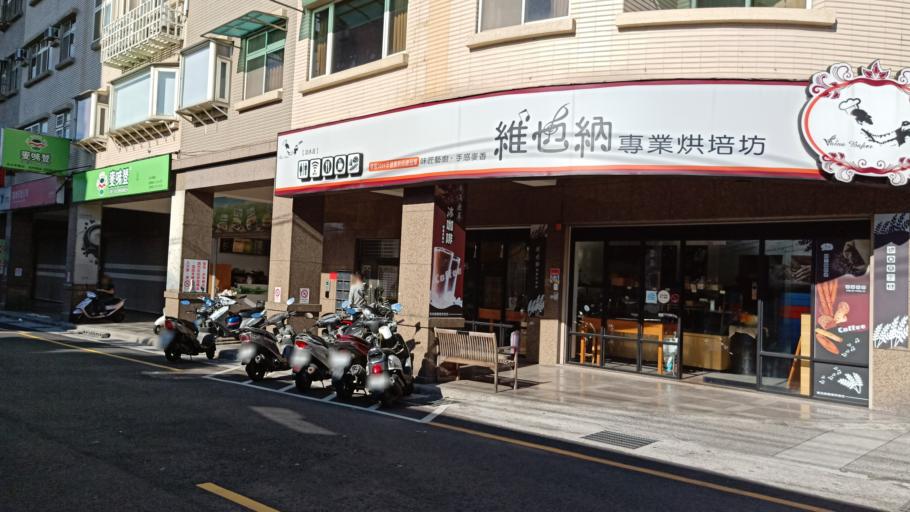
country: TW
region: Taipei
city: Taipei
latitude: 25.1768
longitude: 121.4452
